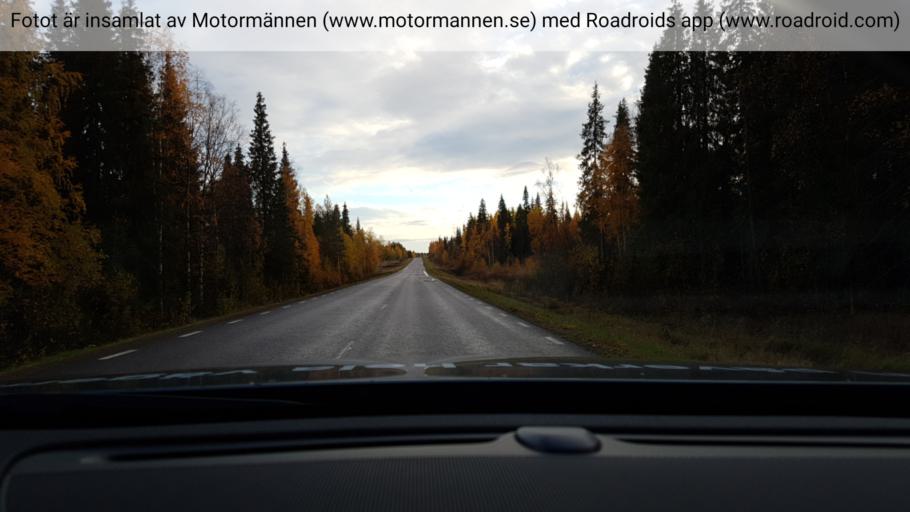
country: SE
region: Norrbotten
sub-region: Overkalix Kommun
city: OEverkalix
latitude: 66.8957
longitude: 22.7723
